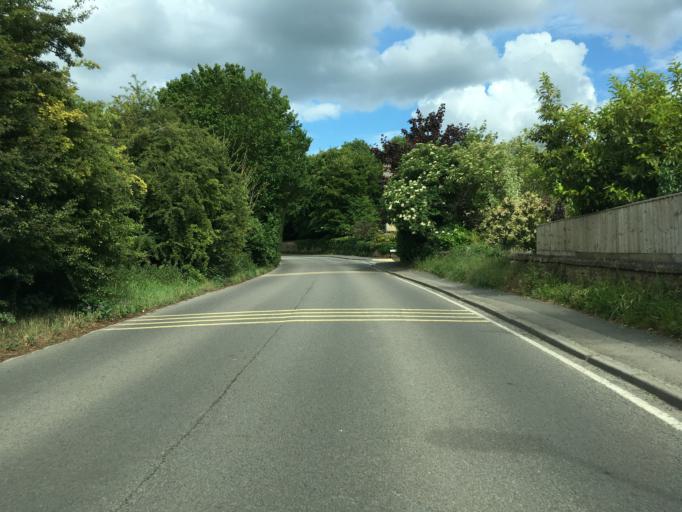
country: GB
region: England
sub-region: Borough of Swindon
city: Broad Blunsdon
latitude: 51.6071
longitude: -1.8060
